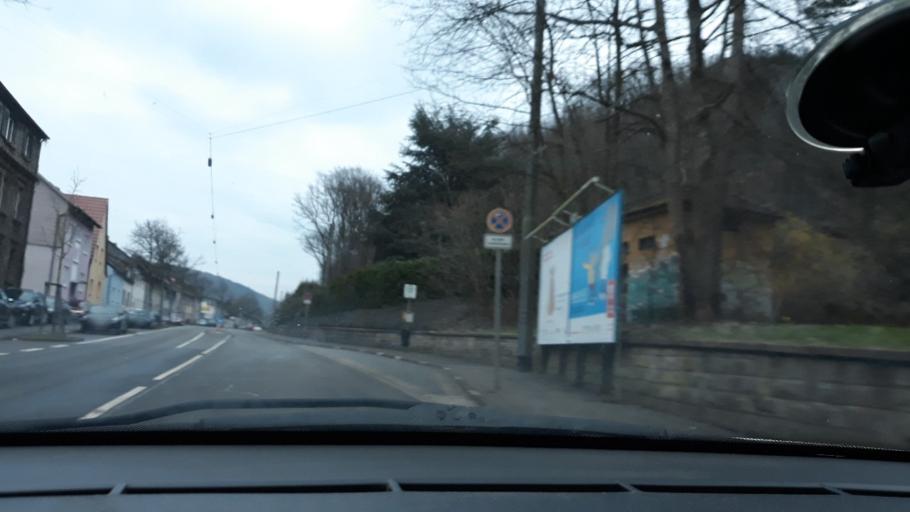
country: DE
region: Saarland
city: Sulzbach
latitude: 49.2372
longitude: 7.0561
